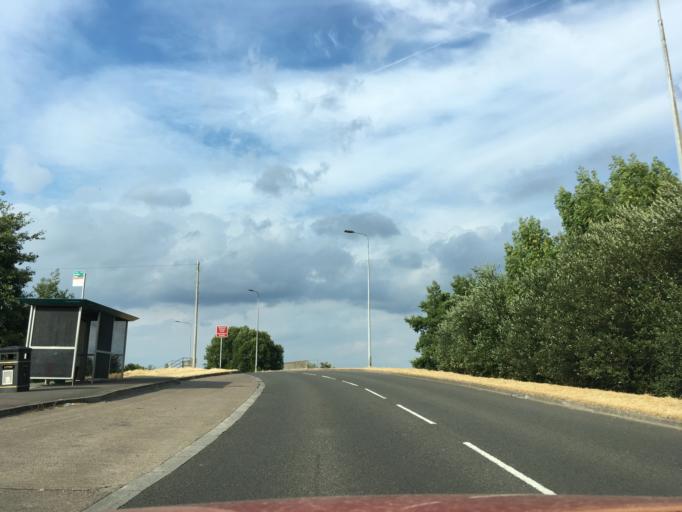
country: GB
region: Wales
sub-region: Newport
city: Marshfield
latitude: 51.5211
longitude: -3.0920
